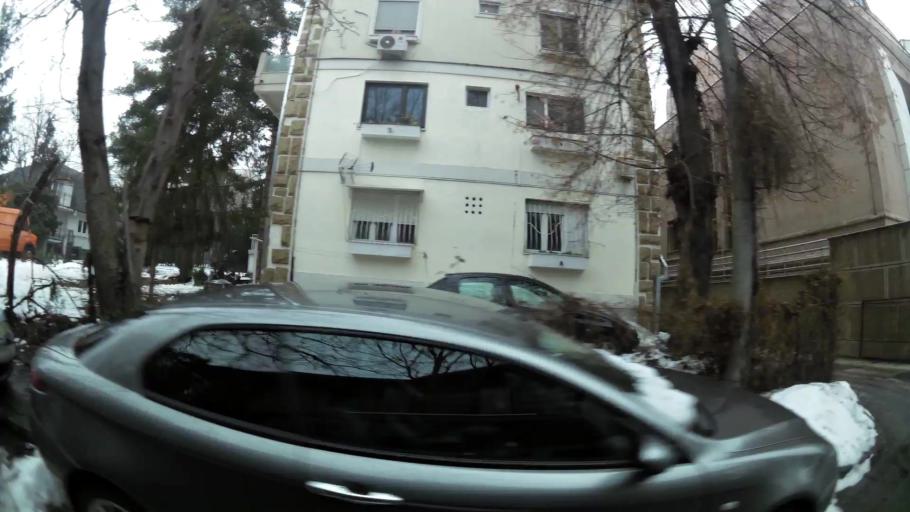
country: RS
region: Central Serbia
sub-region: Belgrade
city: Savski Venac
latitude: 44.7848
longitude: 20.4449
